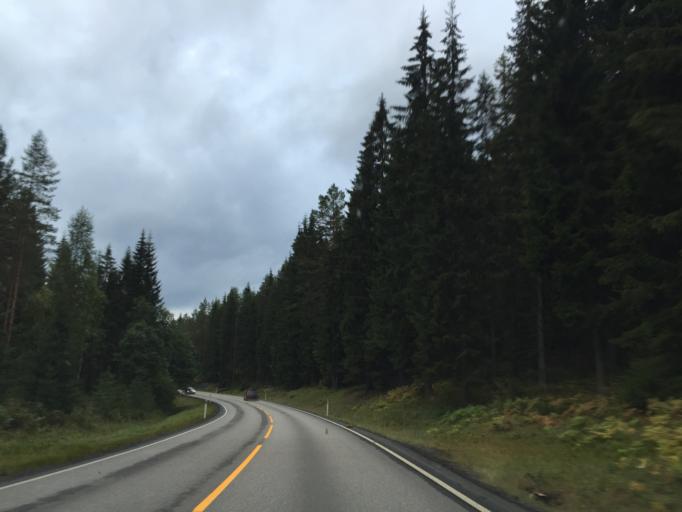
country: NO
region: Hedmark
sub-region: Nord-Odal
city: Sand
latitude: 60.4579
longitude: 11.5088
